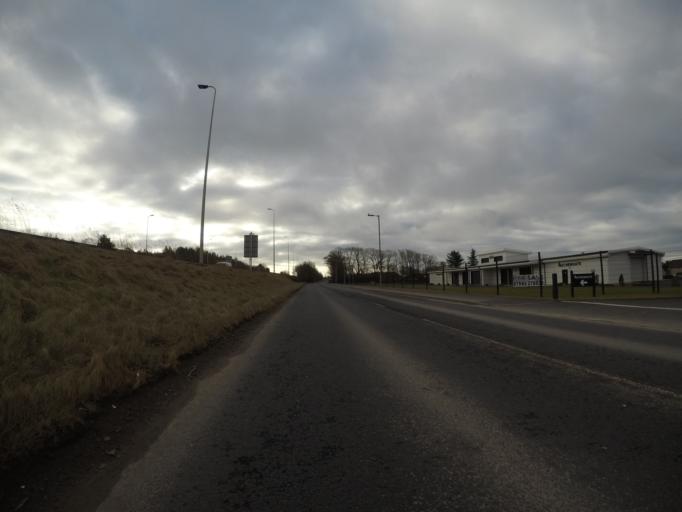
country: GB
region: Scotland
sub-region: North Ayrshire
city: Dreghorn
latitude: 55.5725
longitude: -4.6403
